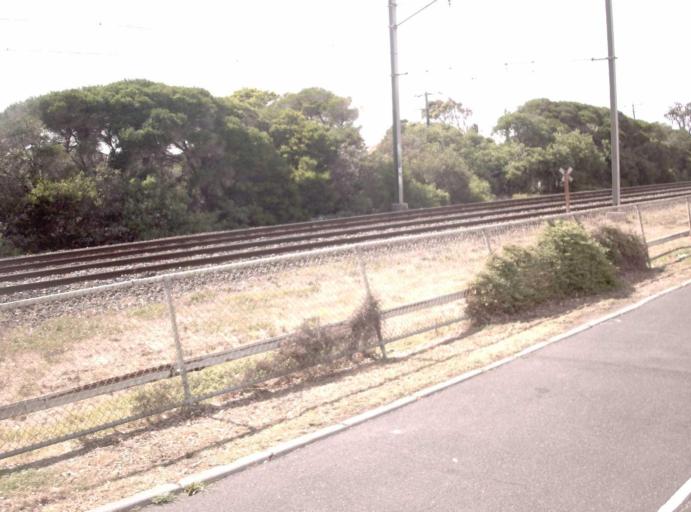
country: AU
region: Victoria
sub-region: Kingston
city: Bonbeach
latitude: -38.0593
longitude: 145.1188
